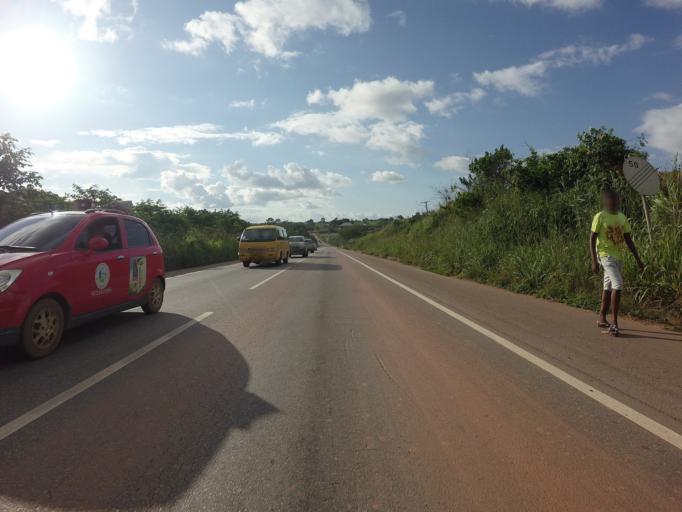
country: GH
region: Ashanti
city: Tafo
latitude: 6.8828
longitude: -1.6439
